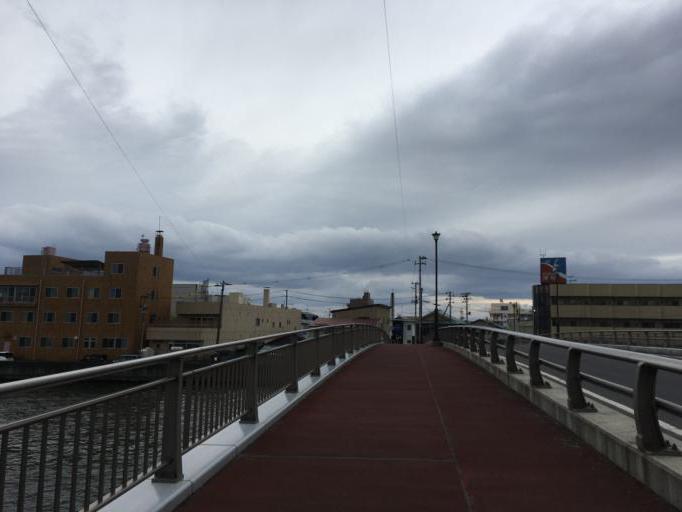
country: JP
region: Aomori
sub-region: Hachinohe Shi
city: Uchimaru
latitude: 40.5235
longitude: 141.5230
